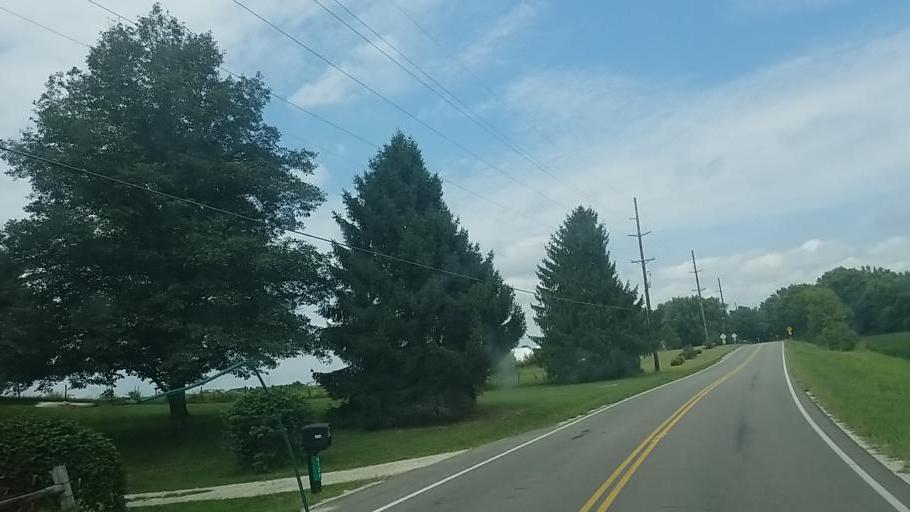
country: US
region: Ohio
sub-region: Franklin County
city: Groveport
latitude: 39.7964
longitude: -82.9023
